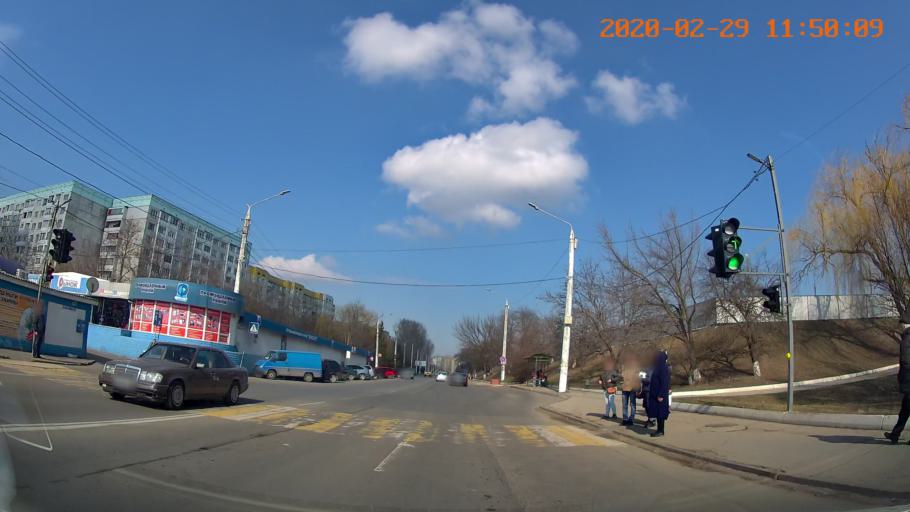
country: MD
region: Telenesti
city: Ribnita
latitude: 47.7561
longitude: 28.9914
